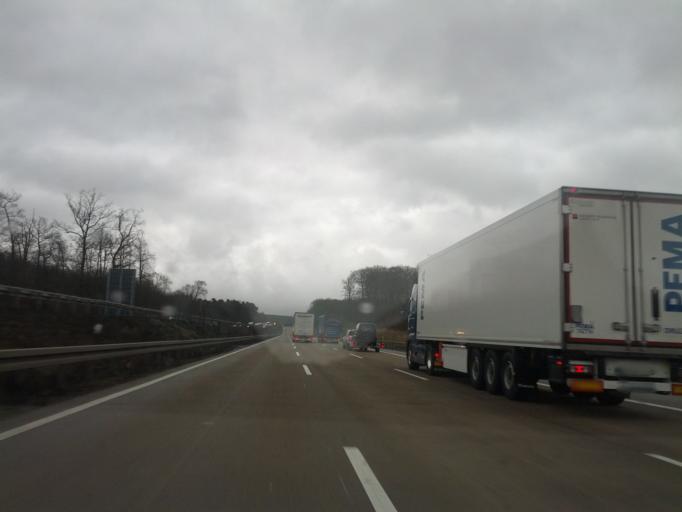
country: DE
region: Hesse
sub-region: Regierungsbezirk Giessen
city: Reiskirchen
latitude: 50.6122
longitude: 8.8356
